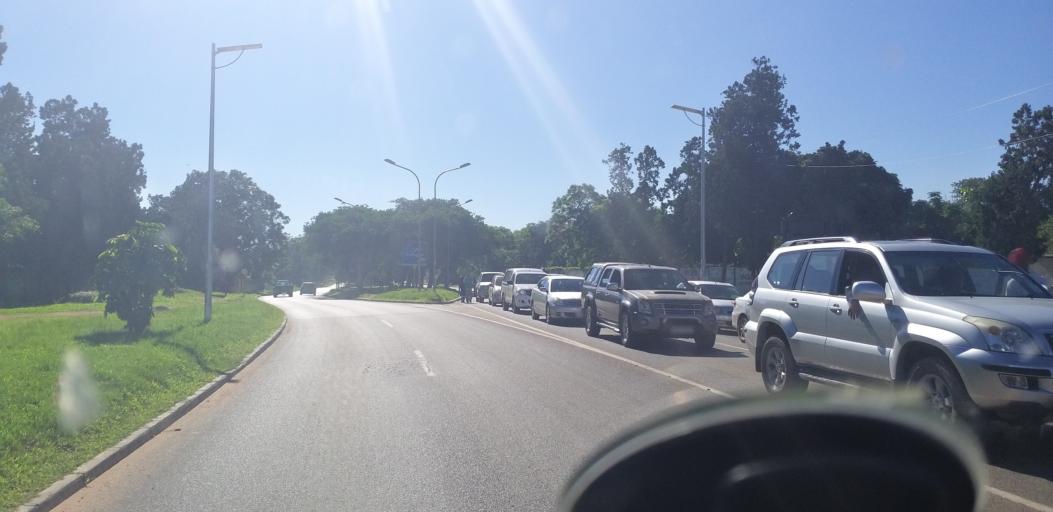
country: ZM
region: Lusaka
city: Lusaka
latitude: -15.4251
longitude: 28.3122
